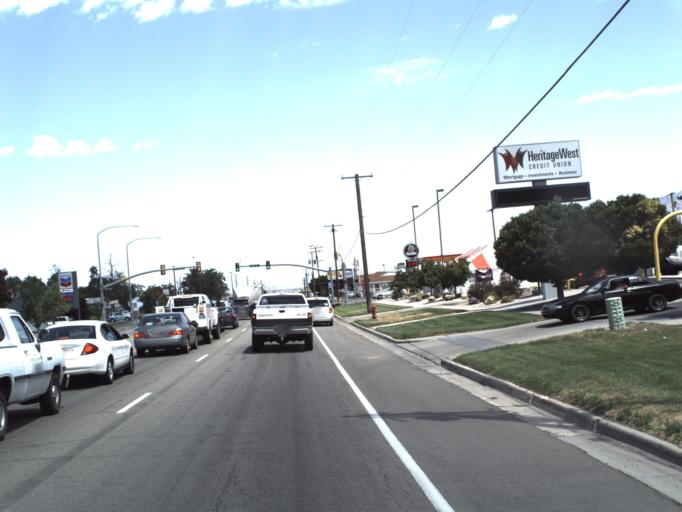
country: US
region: Utah
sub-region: Tooele County
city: Tooele
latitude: 40.5384
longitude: -112.2983
